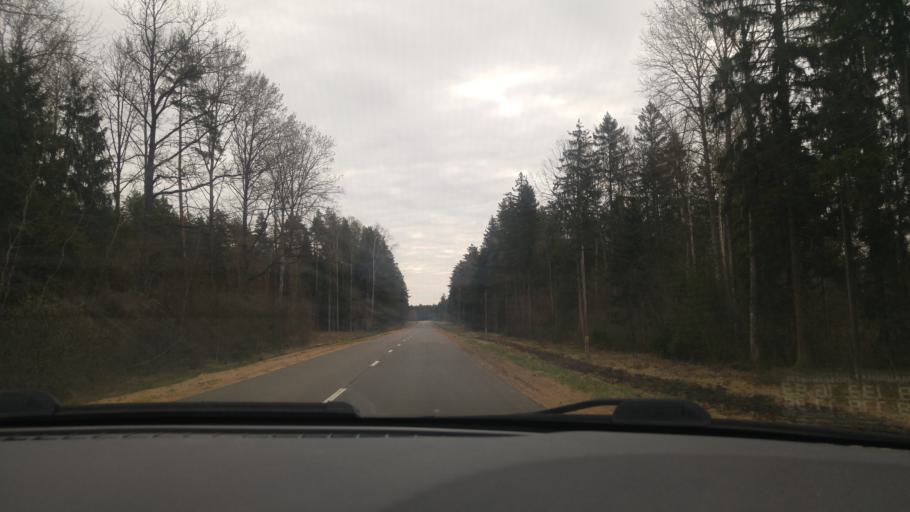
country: BY
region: Minsk
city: Chervyen'
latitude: 53.7331
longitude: 28.2910
